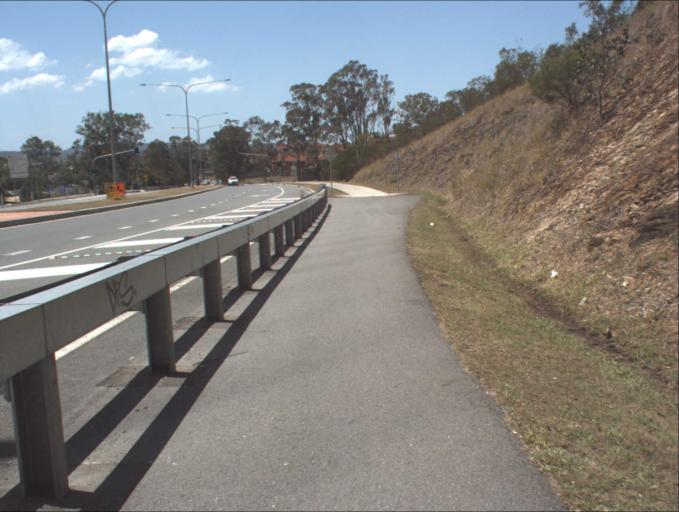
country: AU
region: Queensland
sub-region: Logan
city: Windaroo
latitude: -27.7279
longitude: 153.1926
